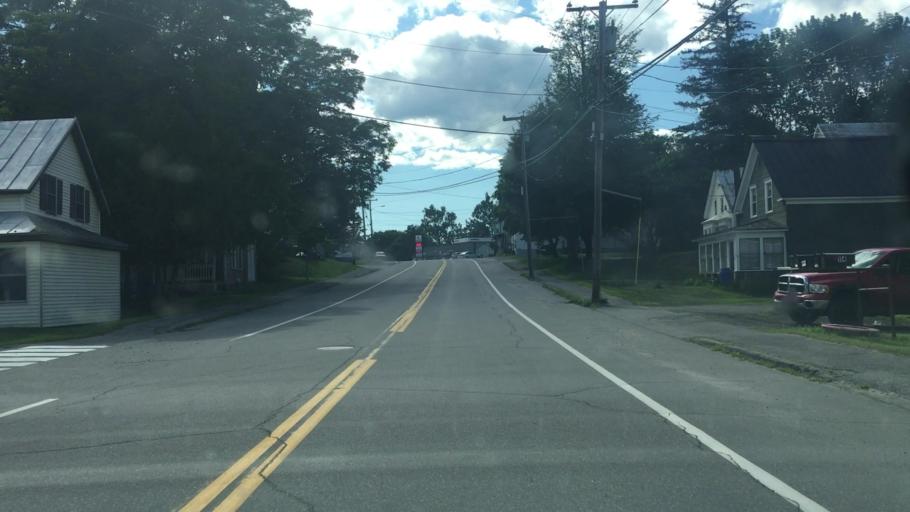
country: US
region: Maine
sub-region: Franklin County
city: Farmington
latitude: 44.6625
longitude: -70.1536
